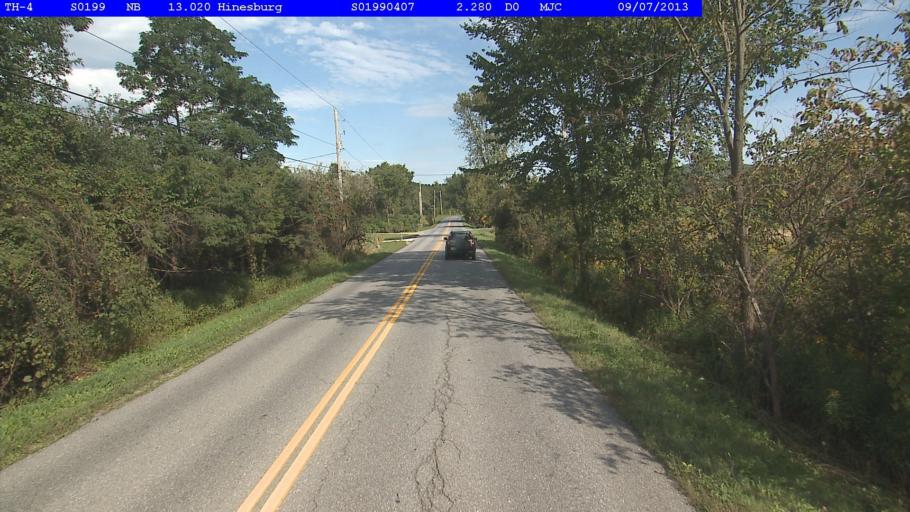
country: US
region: Vermont
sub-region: Chittenden County
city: Hinesburg
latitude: 44.3107
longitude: -73.1099
